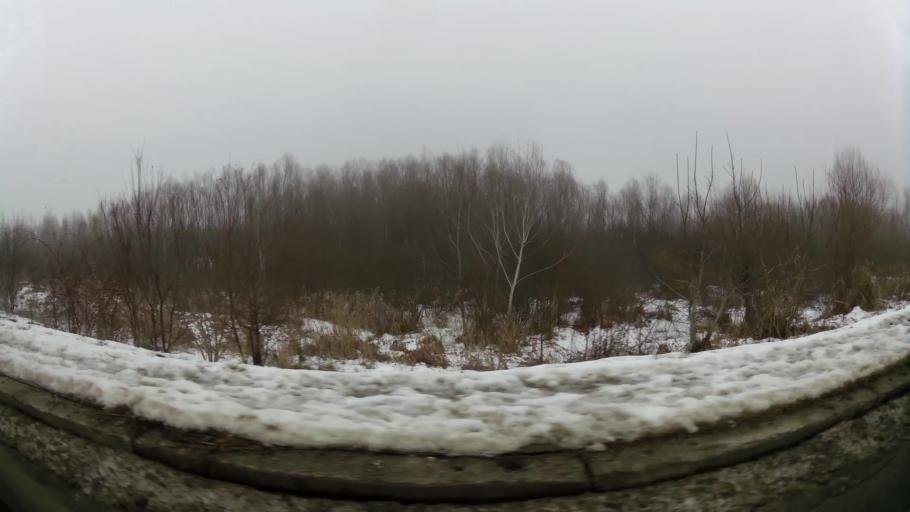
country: RO
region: Ilfov
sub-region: Comuna Chiajna
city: Chiajna
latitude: 44.4607
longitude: 25.9935
